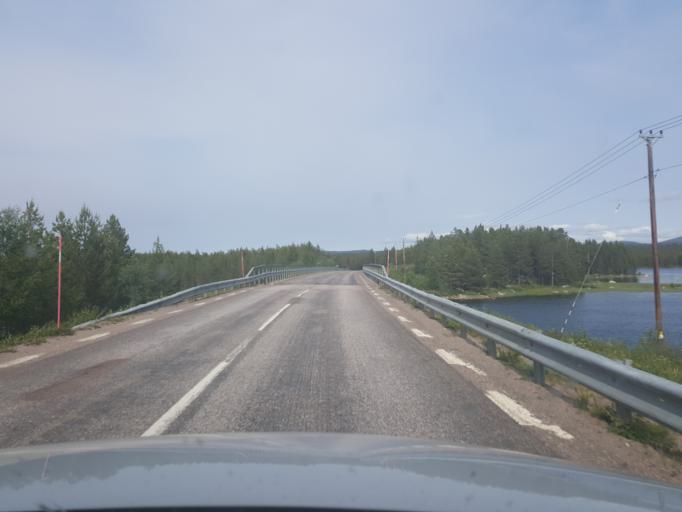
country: SE
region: Norrbotten
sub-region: Arjeplogs Kommun
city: Arjeplog
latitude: 65.8427
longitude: 18.0324
